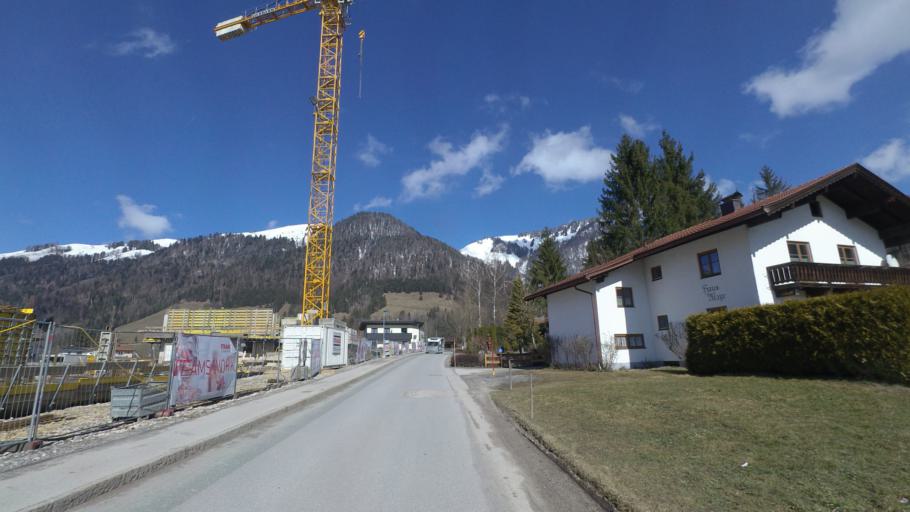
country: AT
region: Tyrol
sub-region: Politischer Bezirk Kufstein
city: Walchsee
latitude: 47.6555
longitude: 12.3185
